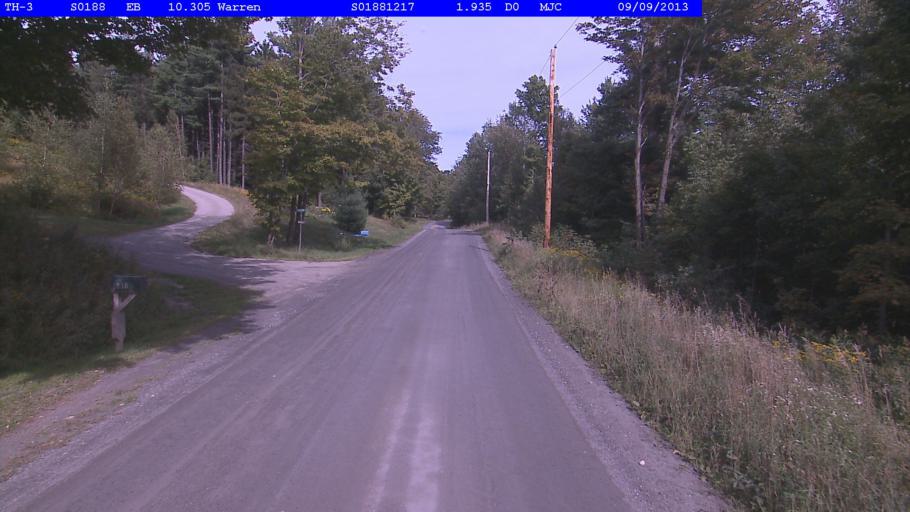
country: US
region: Vermont
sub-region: Addison County
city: Bristol
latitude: 44.1004
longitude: -72.8935
